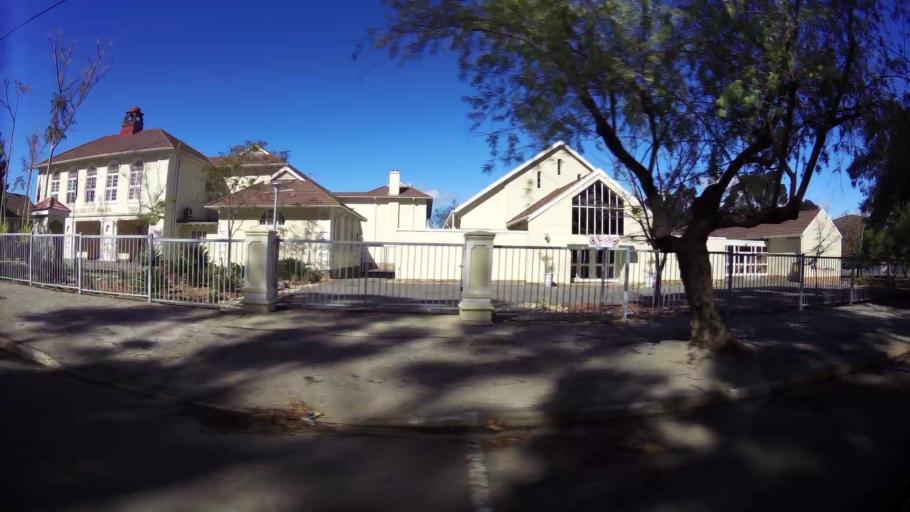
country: ZA
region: Western Cape
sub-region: Cape Winelands District Municipality
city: Ashton
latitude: -33.8073
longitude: 19.8867
